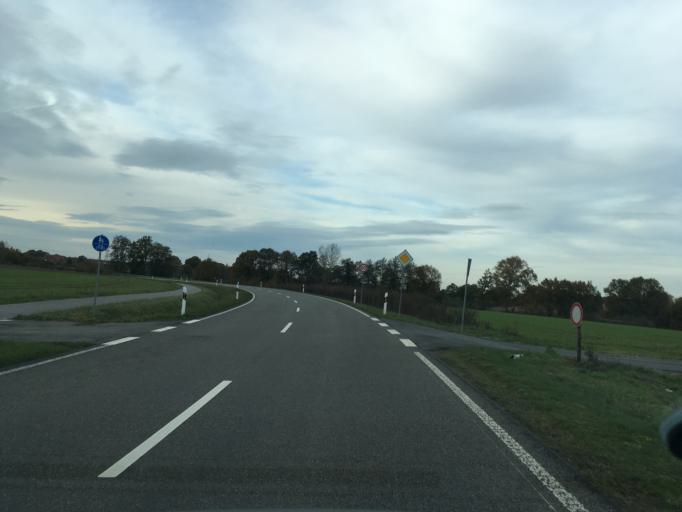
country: DE
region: North Rhine-Westphalia
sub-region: Regierungsbezirk Munster
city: Velen
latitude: 51.8950
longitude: 6.9279
